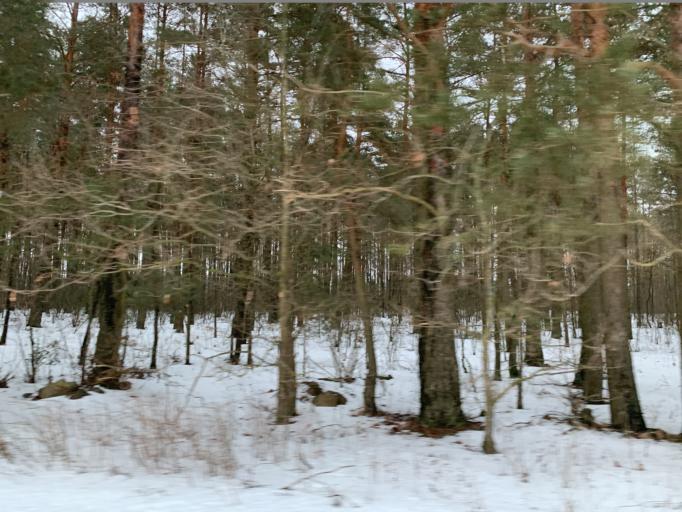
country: BY
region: Minsk
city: Il'ya
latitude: 54.5547
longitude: 27.2834
